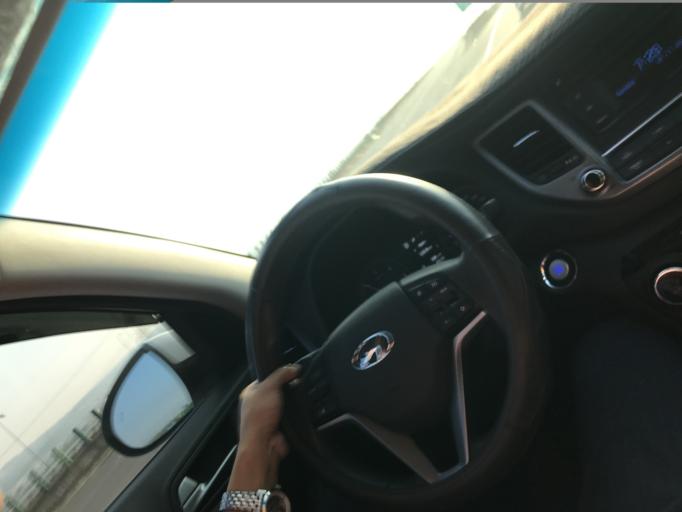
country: TW
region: Taiwan
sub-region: Changhua
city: Chang-hua
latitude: 24.1081
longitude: 120.5510
